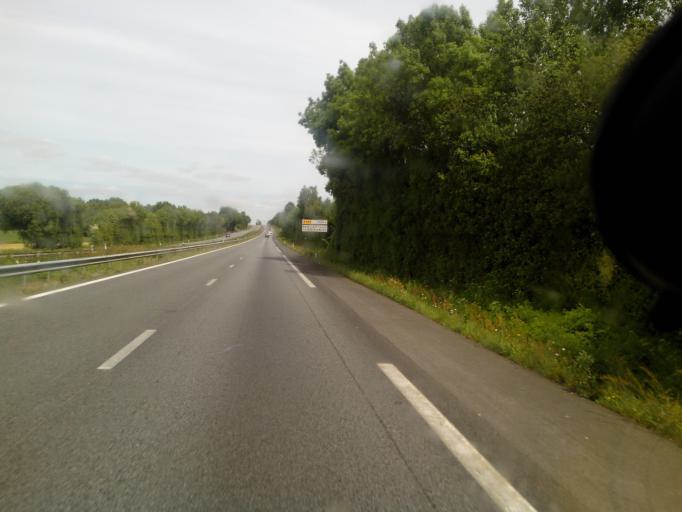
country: FR
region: Brittany
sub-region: Departement d'Ille-et-Vilaine
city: Bain-de-Bretagne
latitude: 47.8158
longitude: -1.6894
